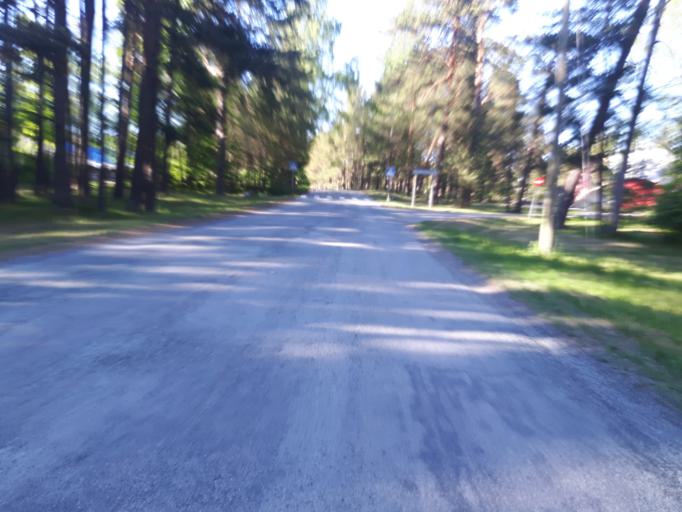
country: EE
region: Harju
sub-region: Loksa linn
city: Loksa
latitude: 59.5770
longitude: 25.9706
